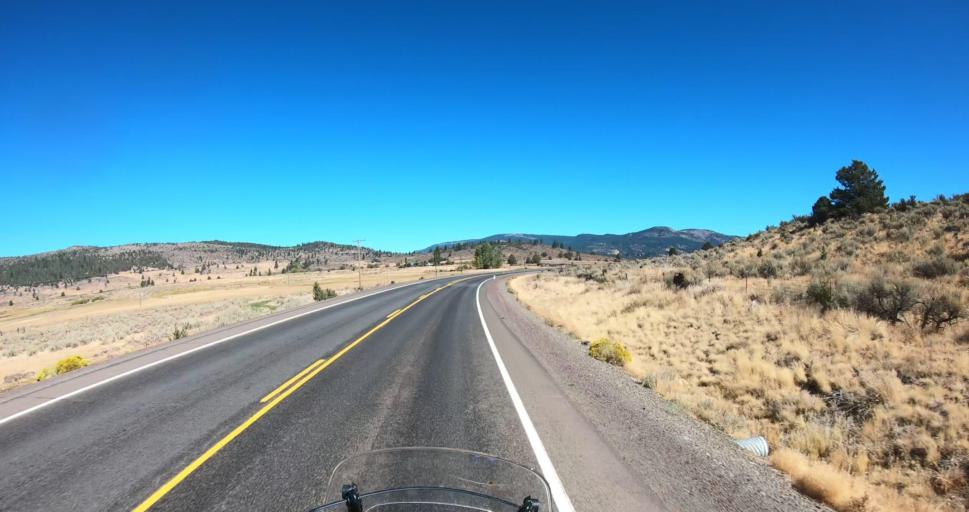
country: US
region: Oregon
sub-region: Lake County
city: Lakeview
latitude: 42.3223
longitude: -120.3303
